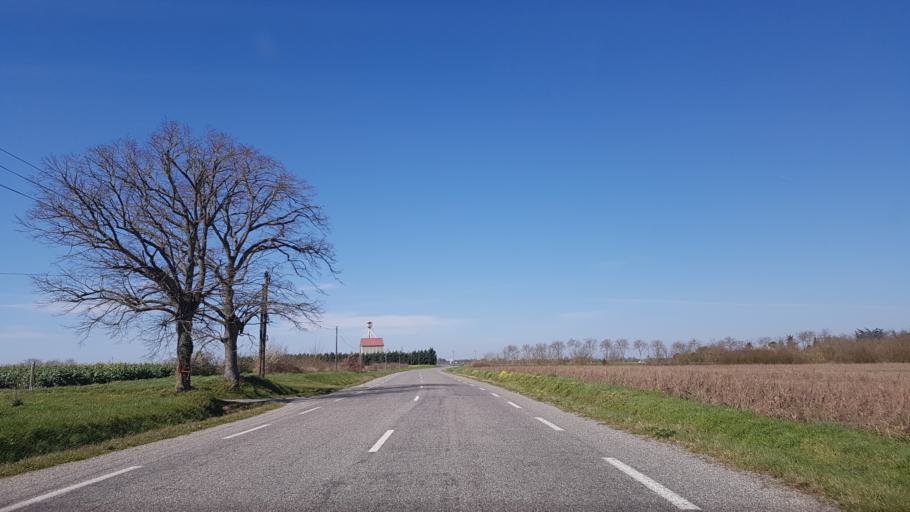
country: FR
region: Midi-Pyrenees
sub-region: Departement de l'Ariege
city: Mazeres
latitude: 43.2327
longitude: 1.6615
